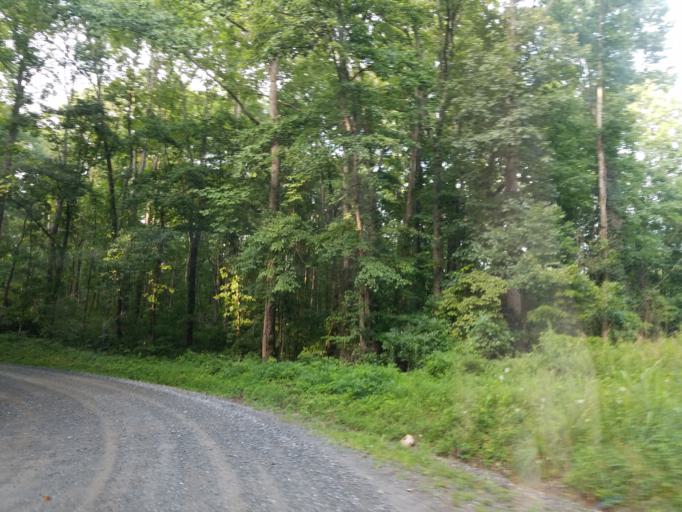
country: US
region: Georgia
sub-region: Pickens County
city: Jasper
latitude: 34.5485
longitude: -84.4381
